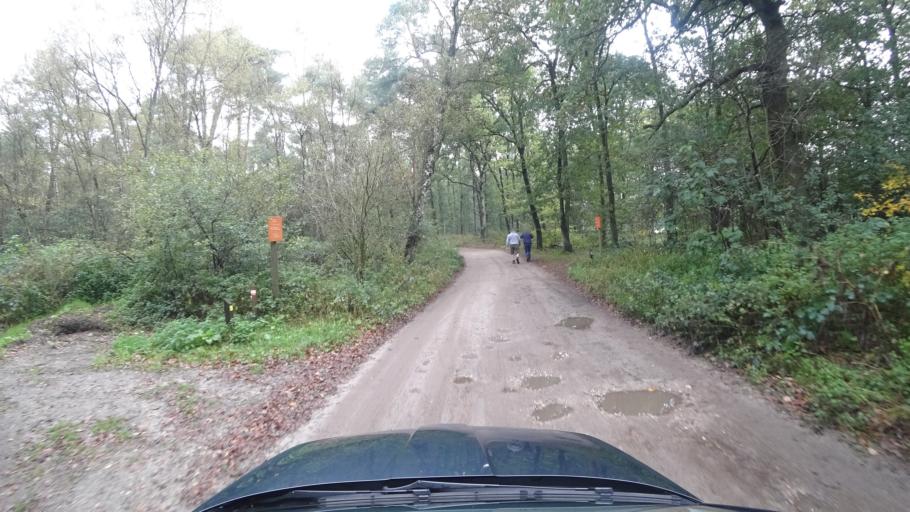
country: NL
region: Gelderland
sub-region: Gemeente Renkum
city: Renkum
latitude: 51.9925
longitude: 5.7287
